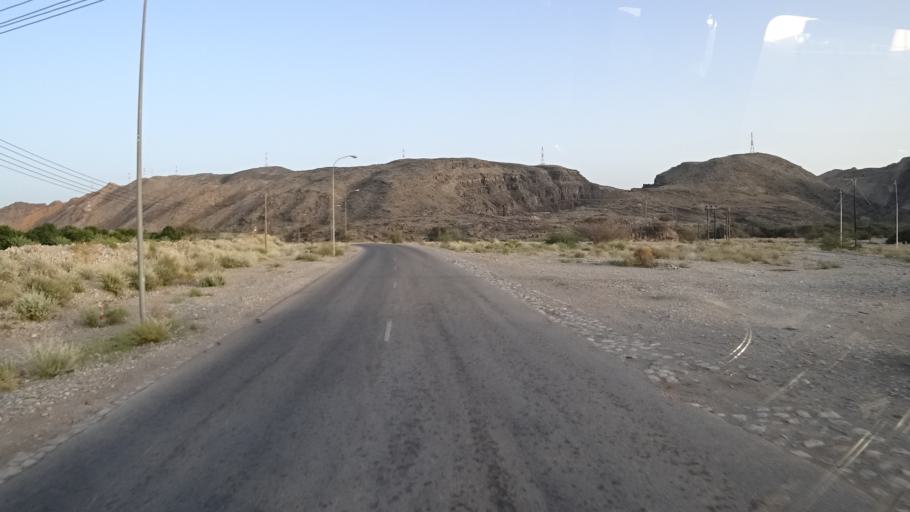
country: OM
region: Muhafazat Masqat
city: Muscat
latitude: 23.5115
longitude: 58.6346
